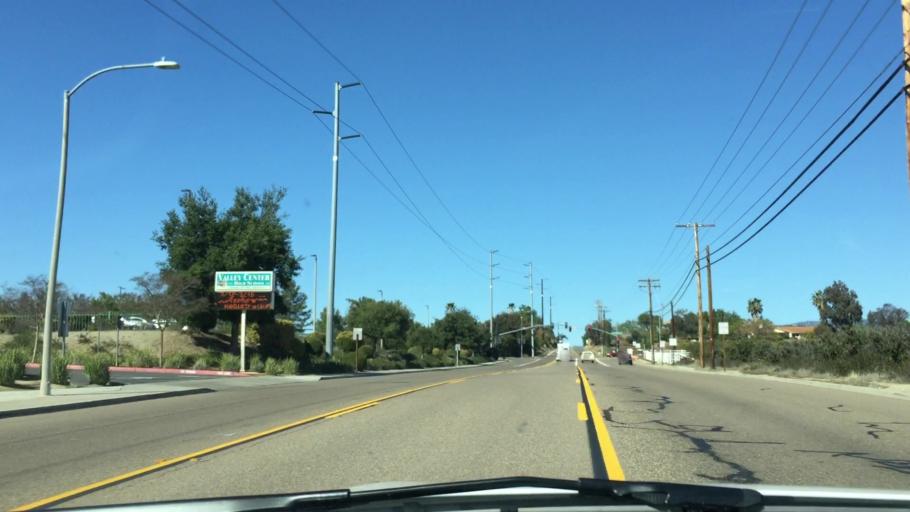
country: US
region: California
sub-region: San Diego County
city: Valley Center
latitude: 33.2801
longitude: -117.0235
